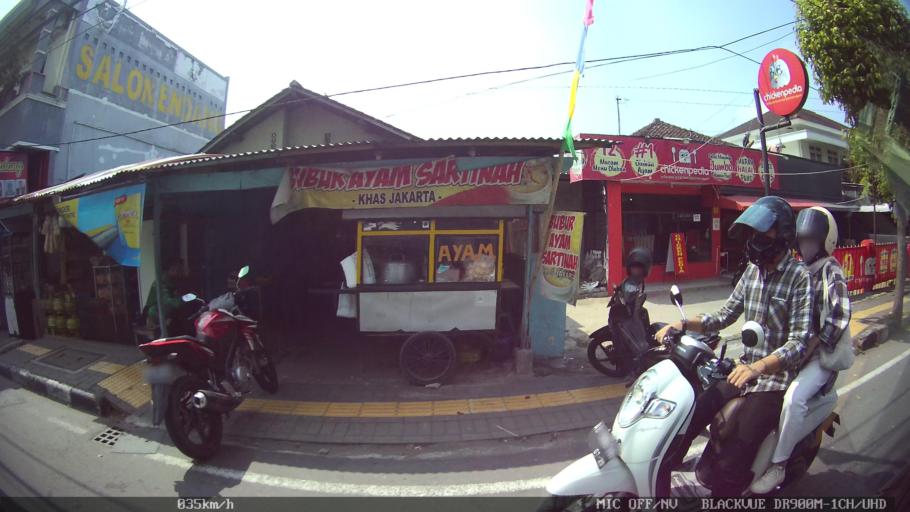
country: ID
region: Daerah Istimewa Yogyakarta
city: Yogyakarta
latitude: -7.8110
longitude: 110.3871
